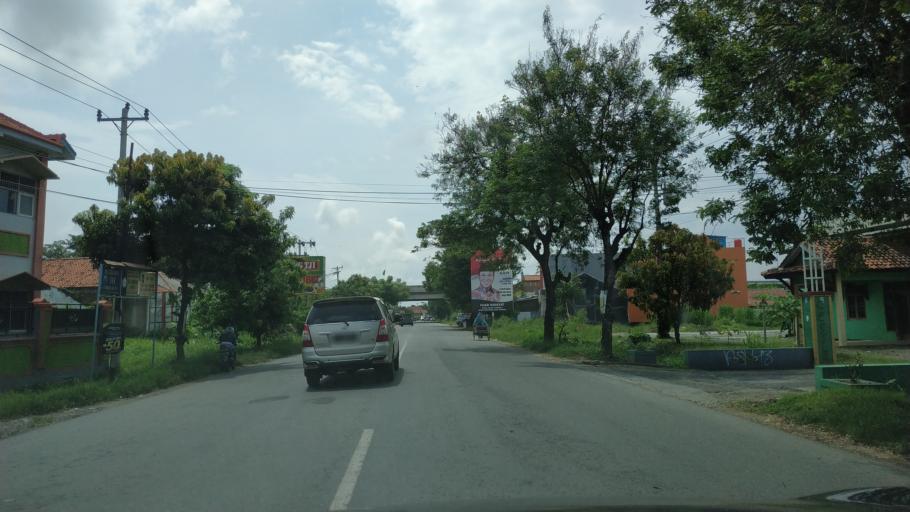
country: ID
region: Central Java
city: Adiwerna
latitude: -6.9365
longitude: 109.1251
